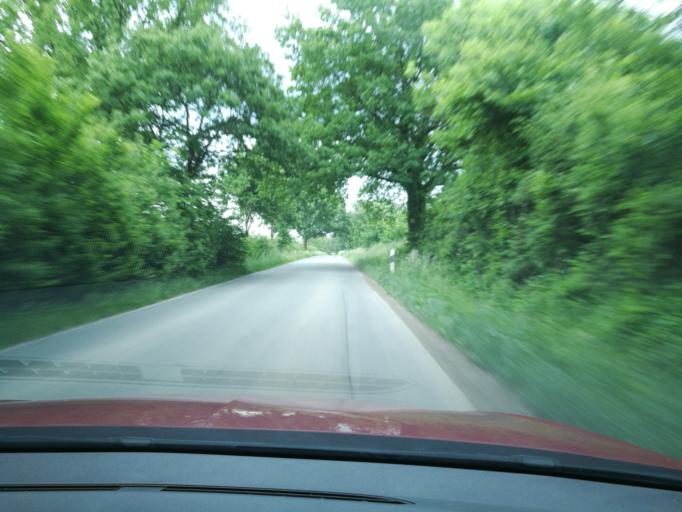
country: DE
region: Schleswig-Holstein
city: Lasbek
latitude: 53.7251
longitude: 10.3507
